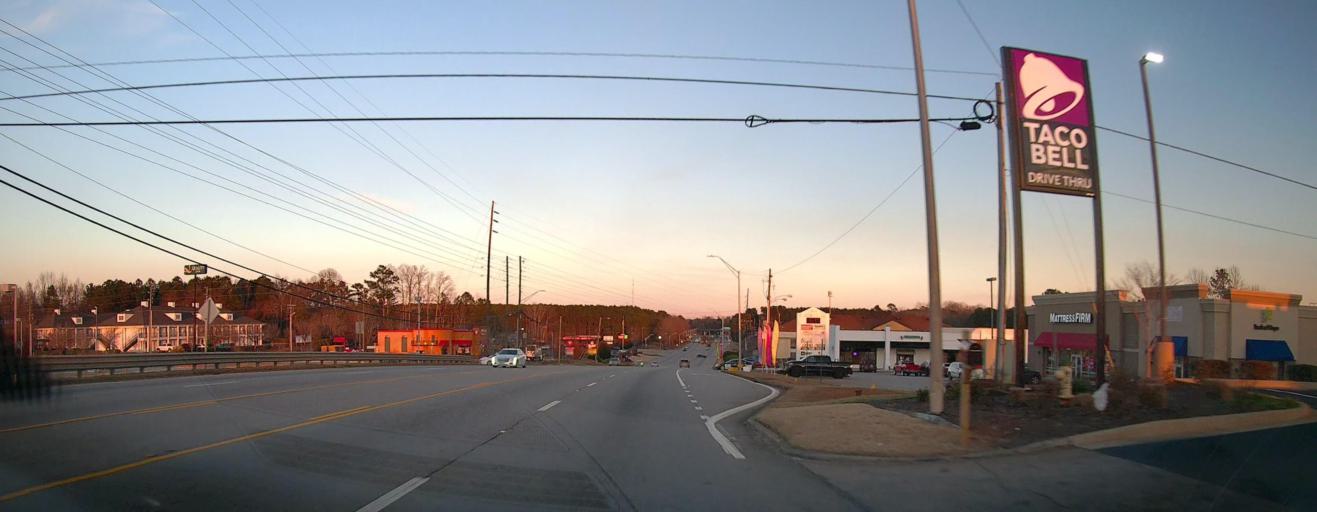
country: US
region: Georgia
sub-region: Troup County
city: La Grange
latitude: 33.0423
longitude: -84.9803
